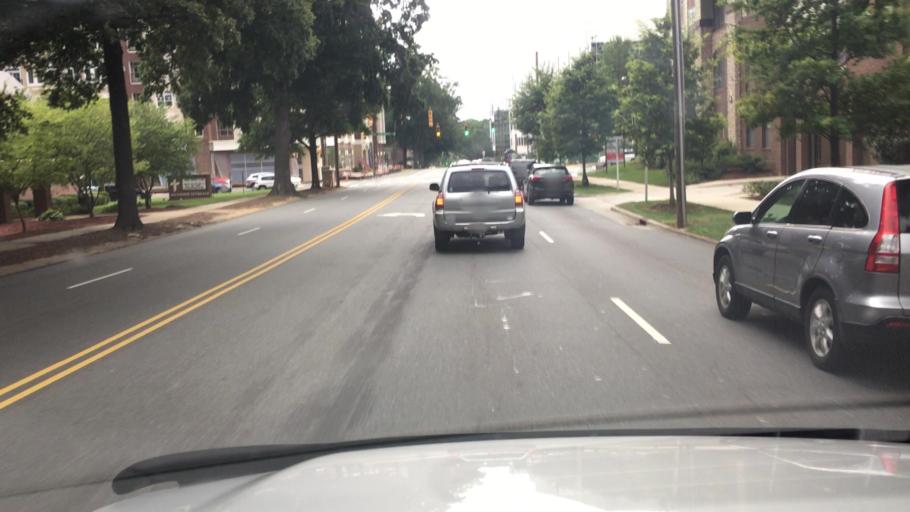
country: US
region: North Carolina
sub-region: Mecklenburg County
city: Charlotte
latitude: 35.2090
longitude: -80.8402
